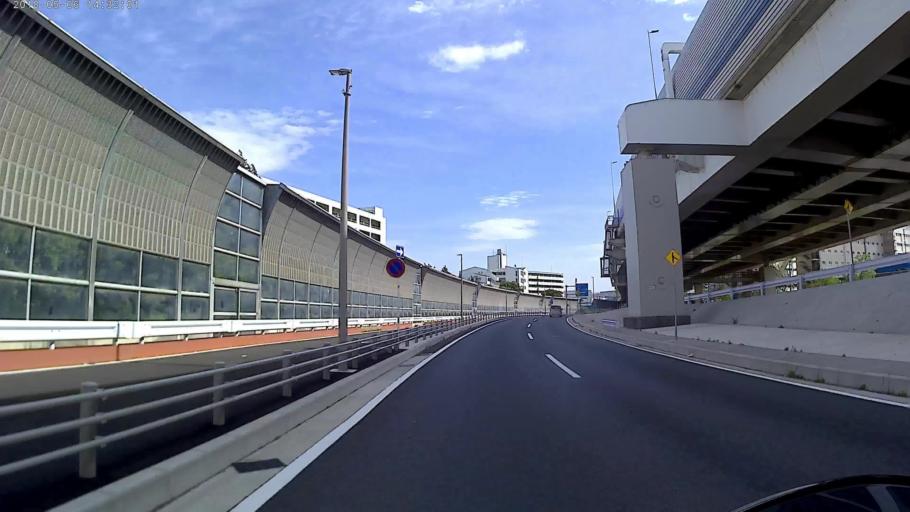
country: JP
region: Kanagawa
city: Yokohama
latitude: 35.4290
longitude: 139.6716
